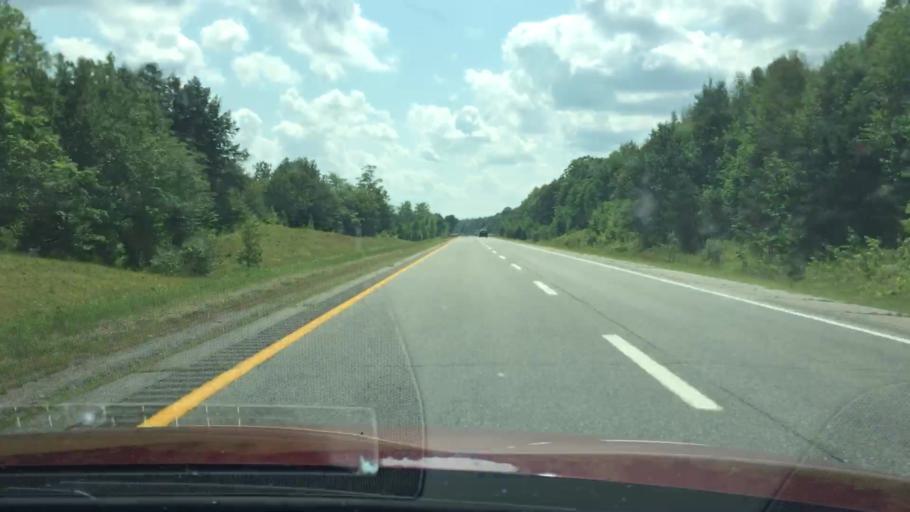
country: US
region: Maine
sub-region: Penobscot County
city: Medway
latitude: 45.5598
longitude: -68.5485
